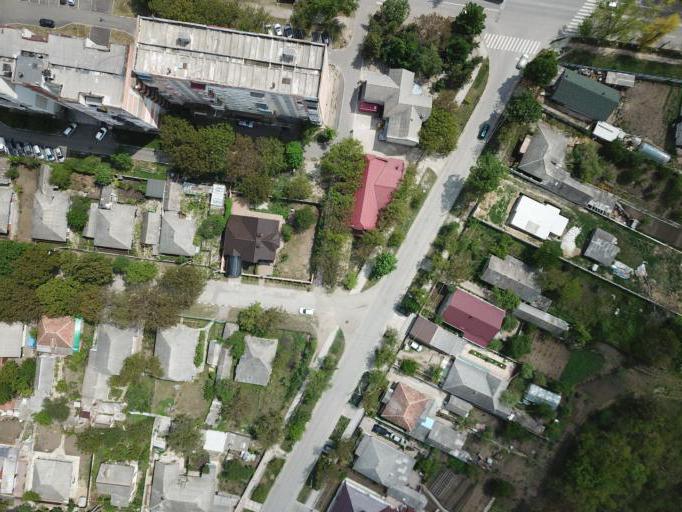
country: MD
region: Ungheni
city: Ungheni
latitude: 47.2082
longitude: 27.7940
